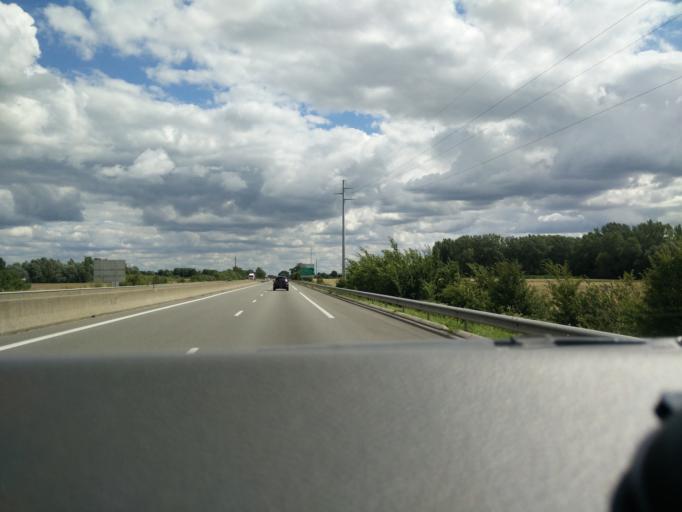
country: FR
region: Nord-Pas-de-Calais
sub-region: Departement du Nord
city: Herzeele
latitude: 50.8758
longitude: 2.5244
